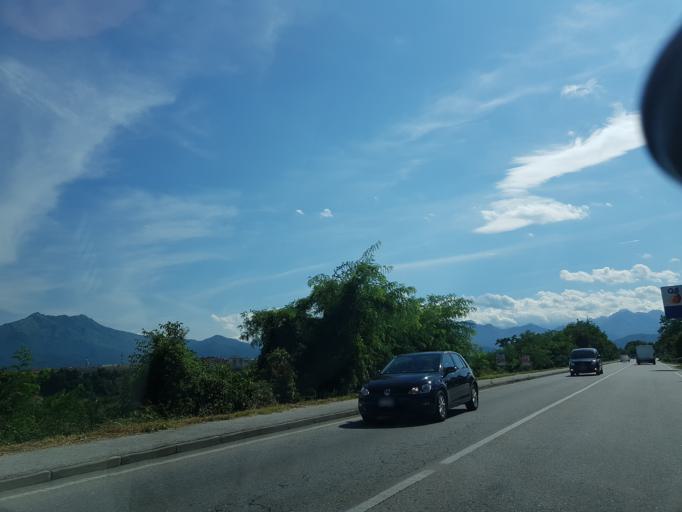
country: IT
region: Piedmont
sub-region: Provincia di Cuneo
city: Cuneo
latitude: 44.4003
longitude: 7.5413
